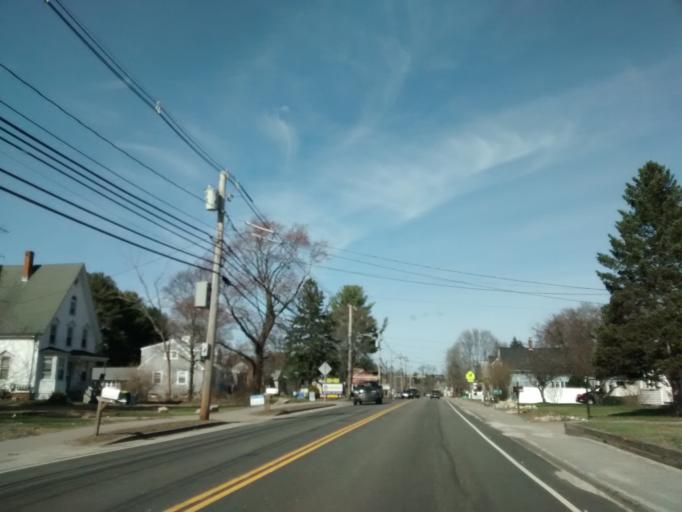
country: US
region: Massachusetts
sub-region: Norfolk County
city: Bellingham
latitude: 42.1198
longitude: -71.4571
